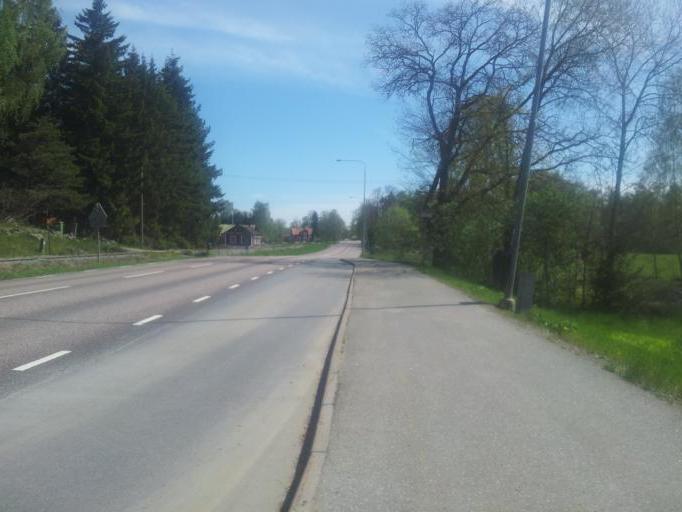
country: SE
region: Stockholm
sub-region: Norrtalje Kommun
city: Nykvarn
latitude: 59.8763
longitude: 18.0387
